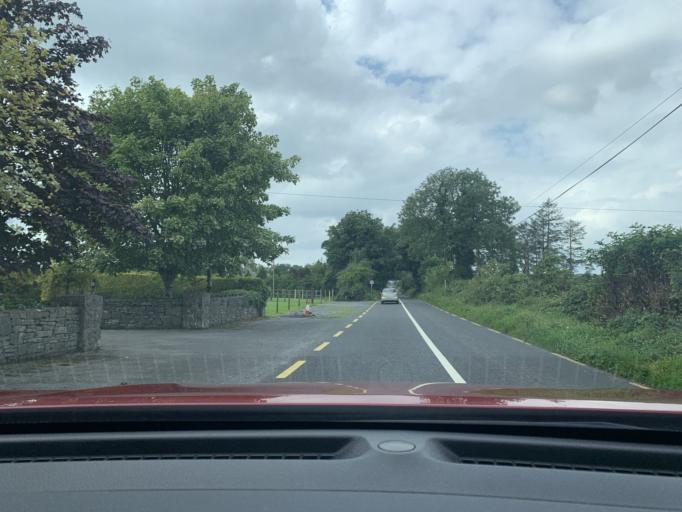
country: IE
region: Connaught
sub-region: Maigh Eo
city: Swinford
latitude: 53.8611
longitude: -8.8559
